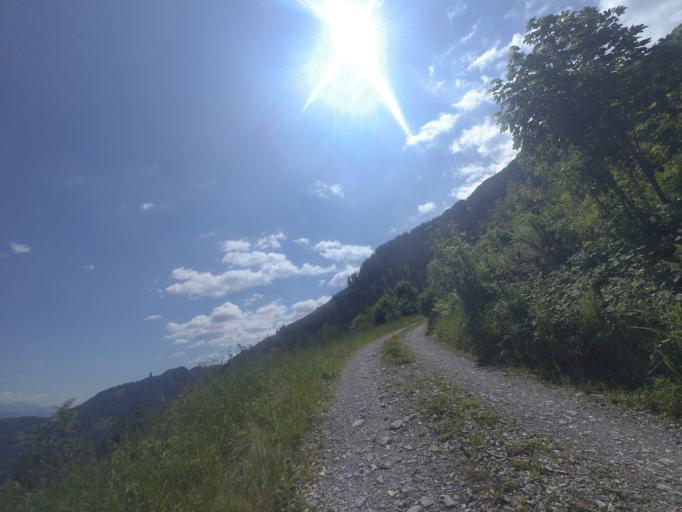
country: AT
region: Salzburg
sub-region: Politischer Bezirk Sankt Johann im Pongau
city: Schwarzach im Pongau
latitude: 47.3030
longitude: 13.1623
